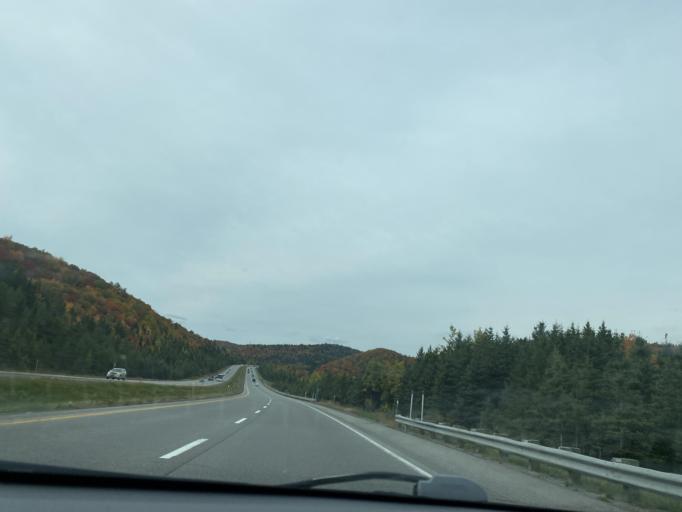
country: CA
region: Quebec
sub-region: Laurentides
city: Val-David
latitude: 45.9905
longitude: -74.1994
